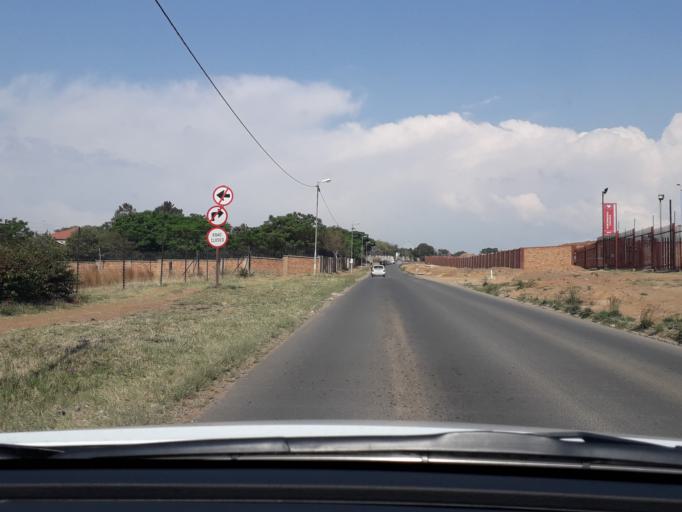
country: ZA
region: Gauteng
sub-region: West Rand District Municipality
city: Muldersdriseloop
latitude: -26.0520
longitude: 27.9407
